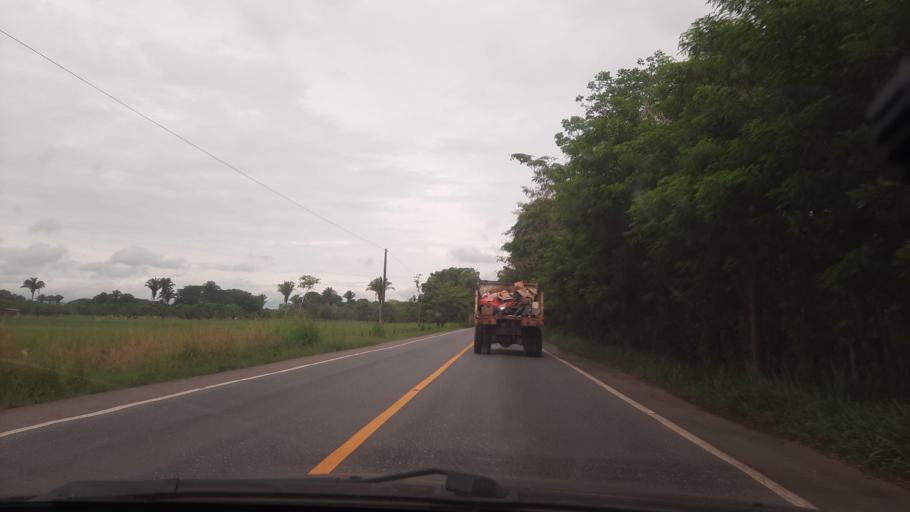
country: GT
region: Izabal
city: Morales
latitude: 15.4699
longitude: -88.9041
